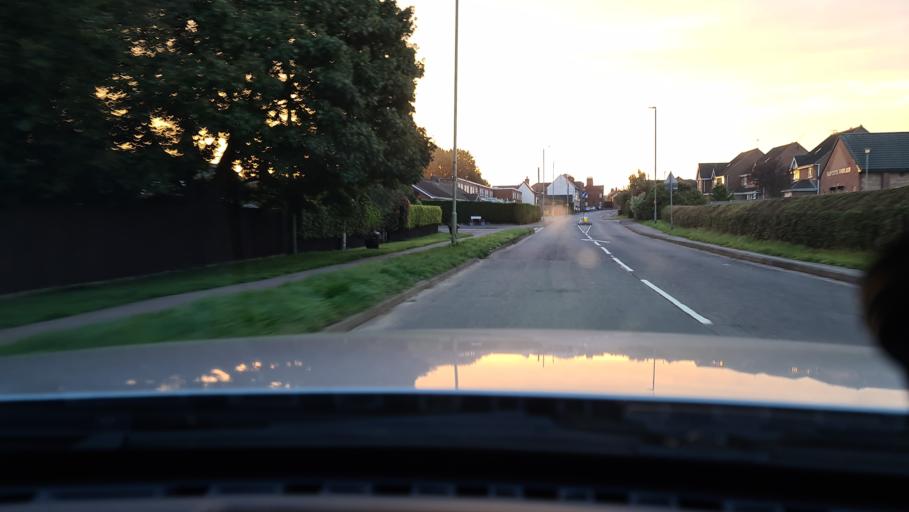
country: GB
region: England
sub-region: Leicestershire
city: Sapcote
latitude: 52.5374
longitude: -1.2841
